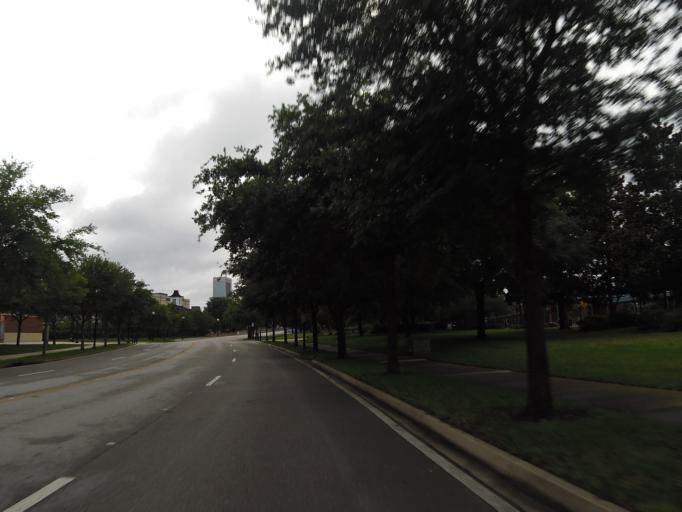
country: US
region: Florida
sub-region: Duval County
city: Jacksonville
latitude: 30.3267
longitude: -81.6448
